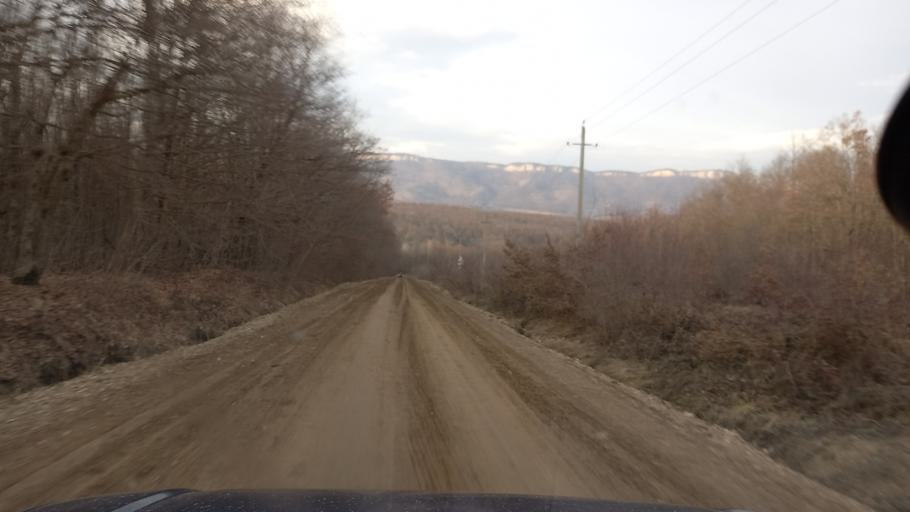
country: RU
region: Adygeya
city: Kamennomostskiy
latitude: 44.1888
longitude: 40.2615
